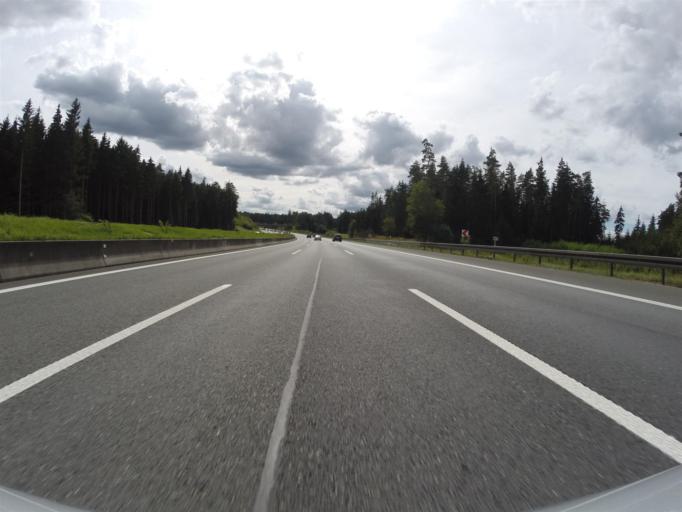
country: DE
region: Bavaria
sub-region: Upper Franconia
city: Pegnitz
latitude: 49.7215
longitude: 11.4846
